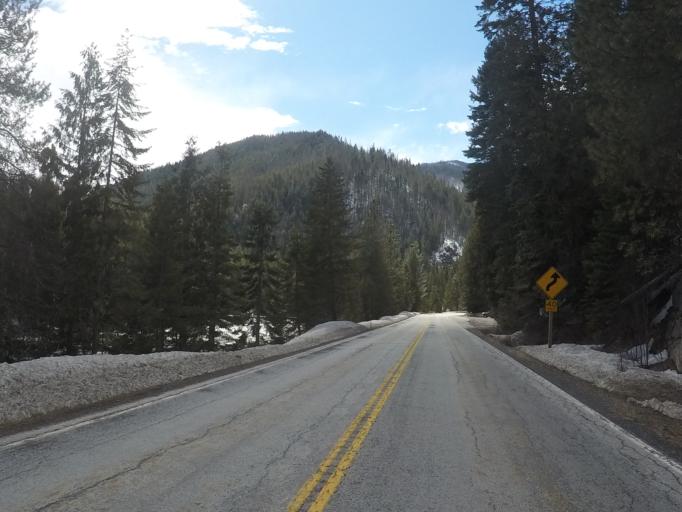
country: US
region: Montana
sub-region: Mineral County
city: Superior
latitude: 46.4763
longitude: -114.8845
